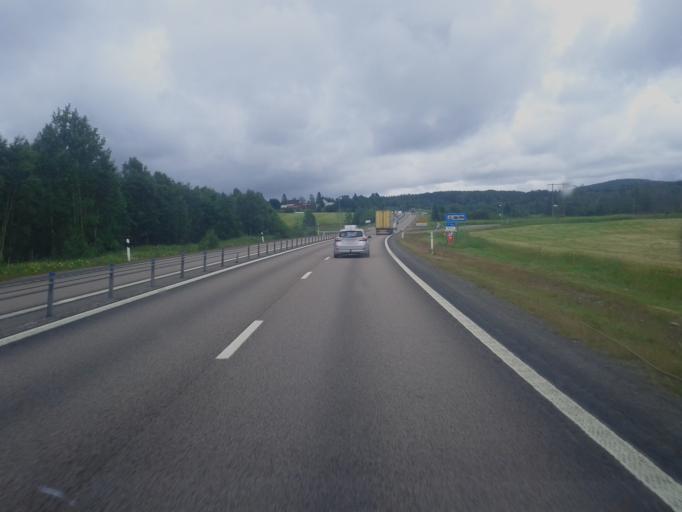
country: SE
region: Vaesternorrland
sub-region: Haernoesands Kommun
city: Haernoesand
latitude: 62.5831
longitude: 17.7706
